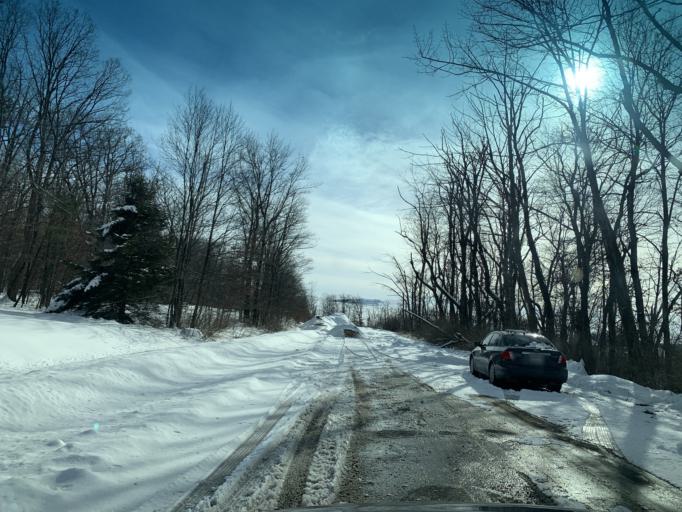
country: US
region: Maryland
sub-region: Allegany County
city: Frostburg
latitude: 39.6187
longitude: -78.9151
